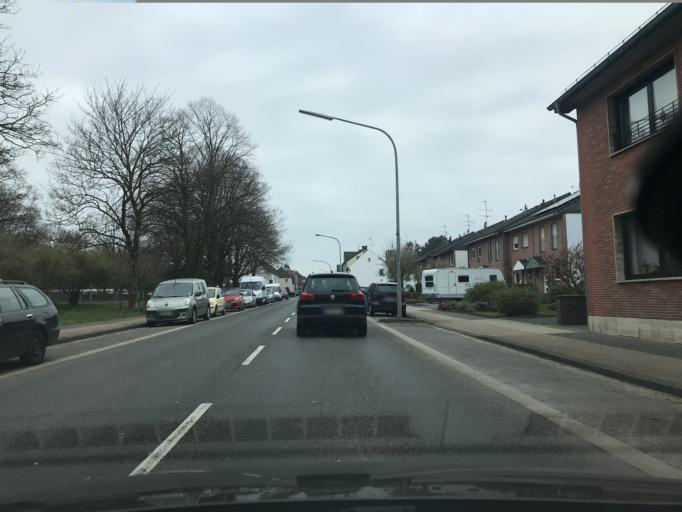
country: DE
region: North Rhine-Westphalia
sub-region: Regierungsbezirk Dusseldorf
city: Viersen
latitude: 51.2650
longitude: 6.3413
